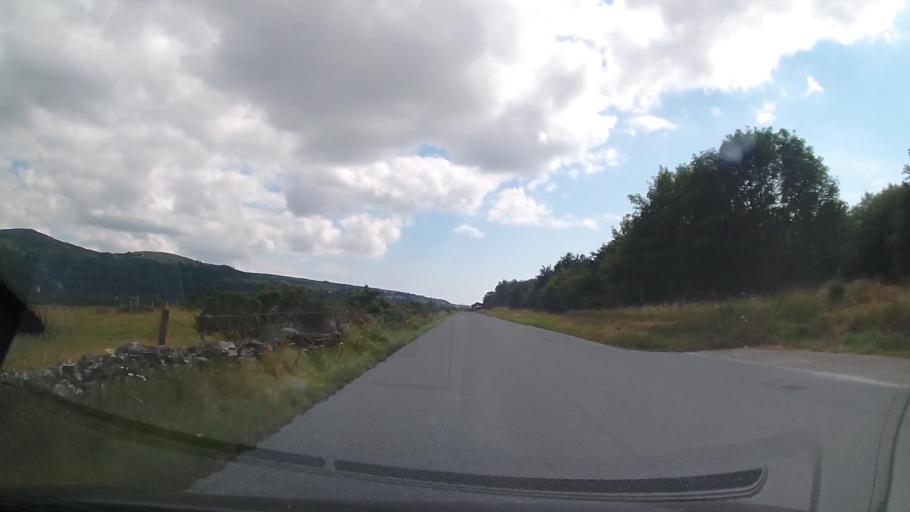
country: GB
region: Wales
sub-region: Gwynedd
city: Llanfair
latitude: 52.8809
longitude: -4.1022
